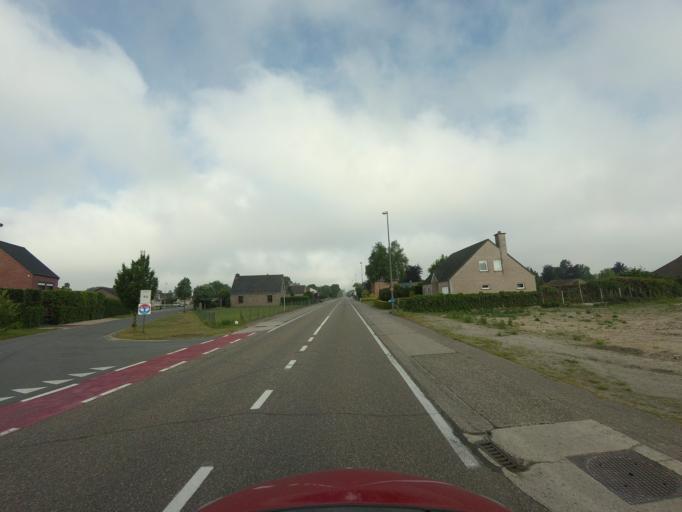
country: BE
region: Flanders
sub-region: Provincie Limburg
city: Lommel
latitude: 51.2242
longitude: 5.3347
